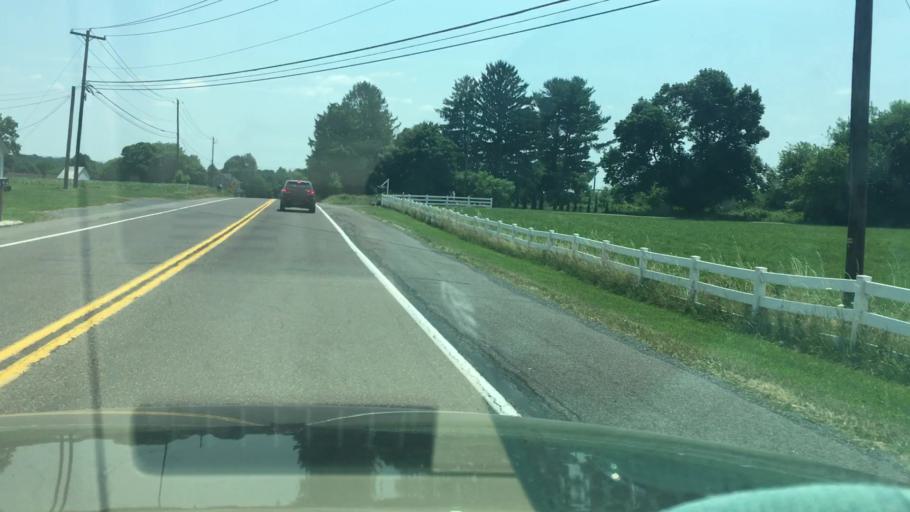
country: US
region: Pennsylvania
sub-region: Lehigh County
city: Schnecksville
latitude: 40.6098
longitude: -75.6477
